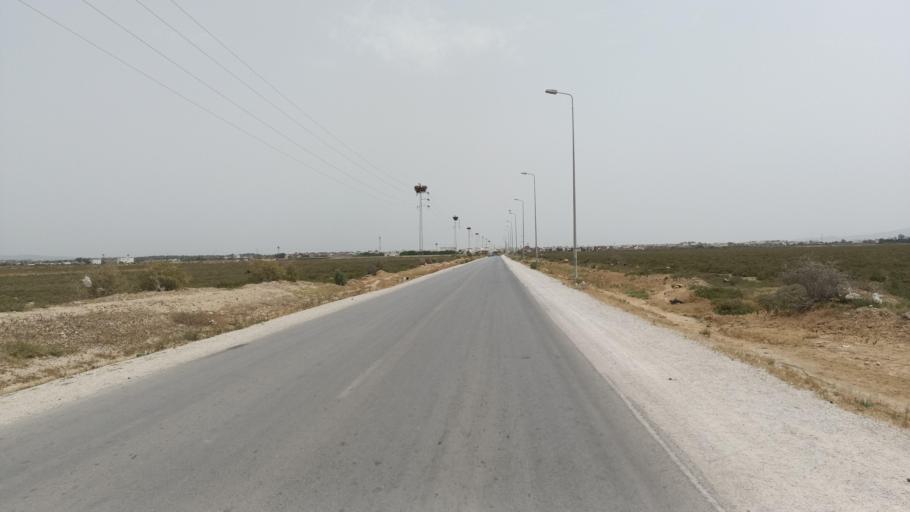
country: TN
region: Nabul
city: Manzil Bu Zalafah
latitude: 36.7194
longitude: 10.4755
